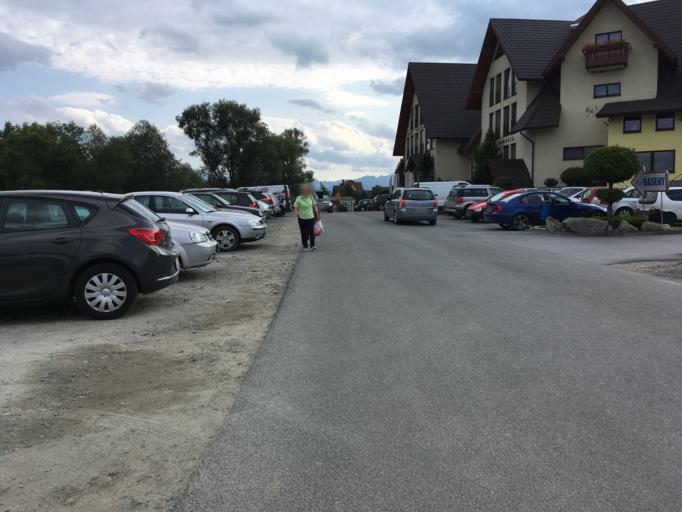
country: PL
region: Lesser Poland Voivodeship
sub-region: Powiat tatrzanski
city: Bialy Dunajec
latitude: 49.3984
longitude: 20.0212
